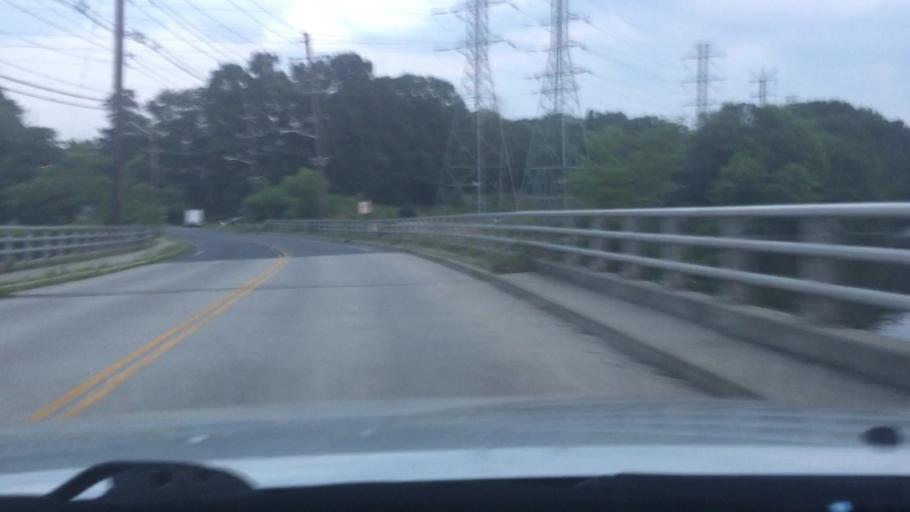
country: US
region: New Jersey
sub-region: Middlesex County
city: Milltown
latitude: 40.4399
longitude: -74.4672
